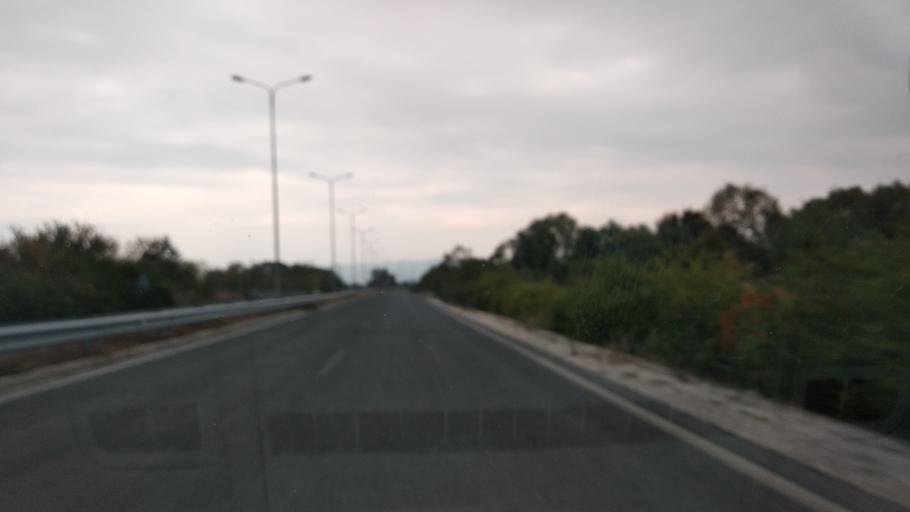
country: GR
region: Thessaly
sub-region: Trikala
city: Pyrgetos
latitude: 39.5685
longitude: 21.7405
